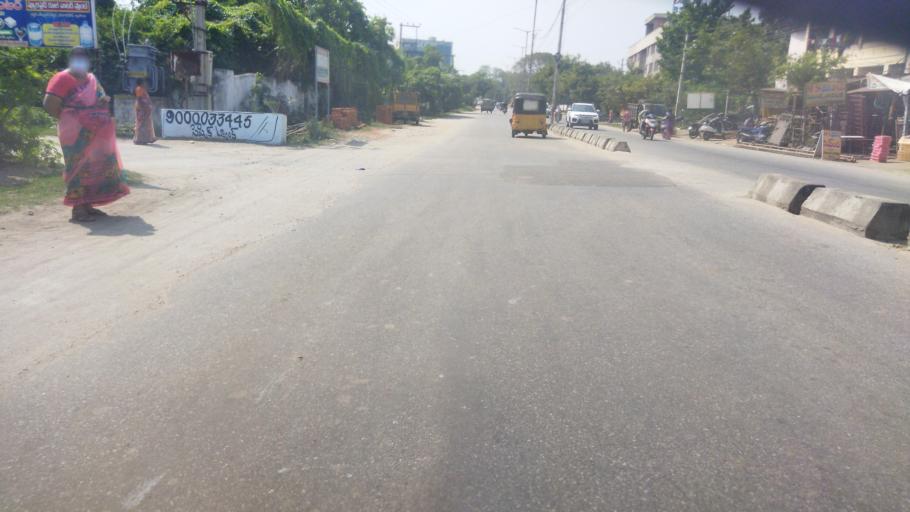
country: IN
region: Telangana
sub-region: Nalgonda
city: Nalgonda
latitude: 17.0716
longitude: 79.2842
